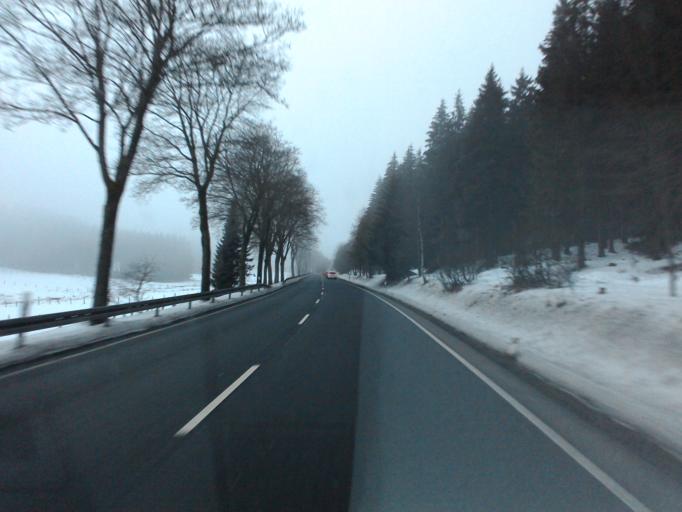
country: DE
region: North Rhine-Westphalia
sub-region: Regierungsbezirk Arnsberg
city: Winterberg
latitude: 51.2231
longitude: 8.5392
